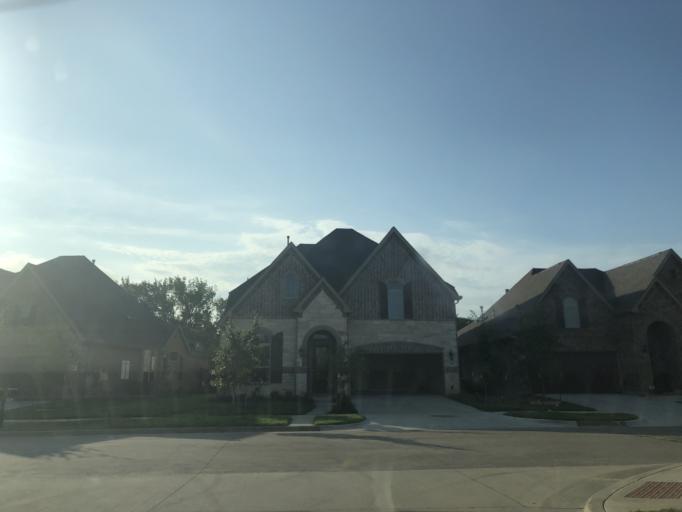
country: US
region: Texas
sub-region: Tarrant County
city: Euless
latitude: 32.8482
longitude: -97.0678
